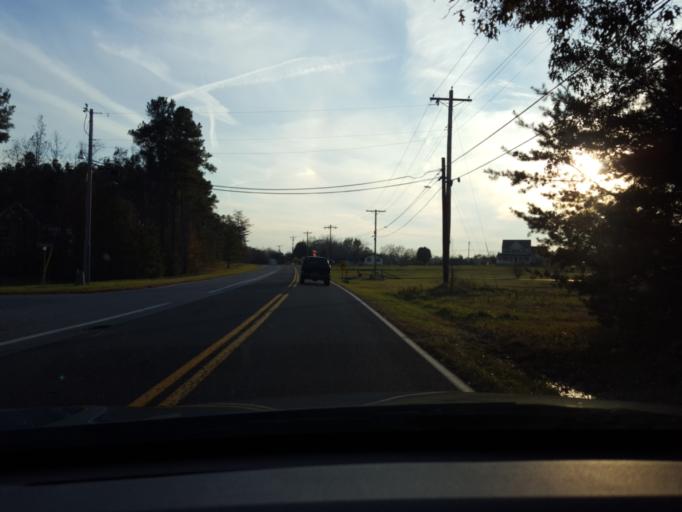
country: US
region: Maryland
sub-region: Charles County
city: Hughesville
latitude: 38.5081
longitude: -76.8632
